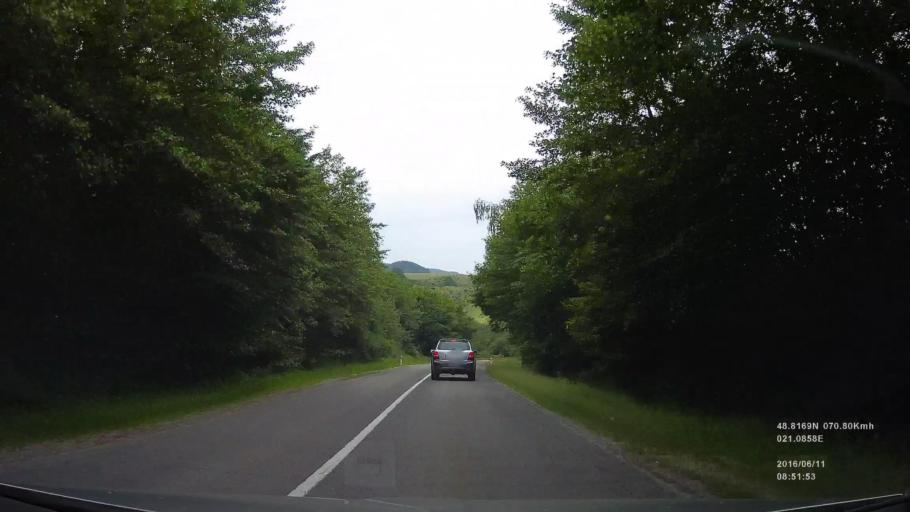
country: SK
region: Kosicky
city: Gelnica
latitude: 48.8132
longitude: 21.0928
